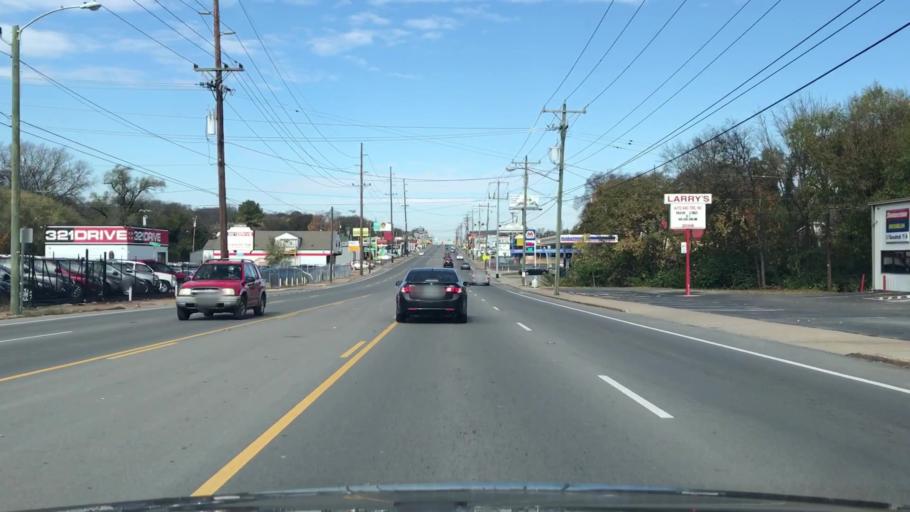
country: US
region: Tennessee
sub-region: Davidson County
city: Oak Hill
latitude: 36.0973
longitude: -86.7382
